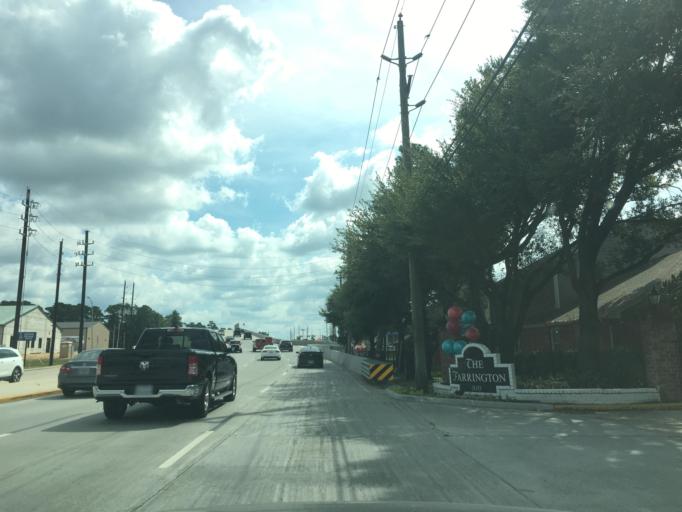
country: US
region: Texas
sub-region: Montgomery County
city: Oak Ridge North
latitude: 30.1273
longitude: -95.4322
